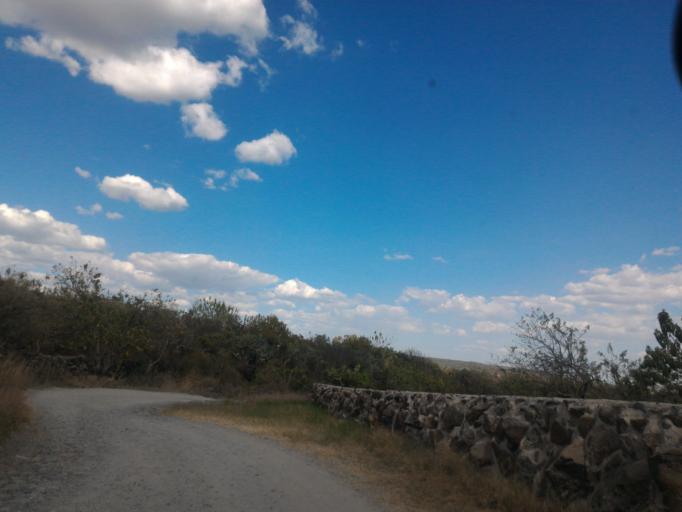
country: MX
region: Jalisco
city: San Diego de Alejandria
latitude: 20.8854
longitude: -101.9910
